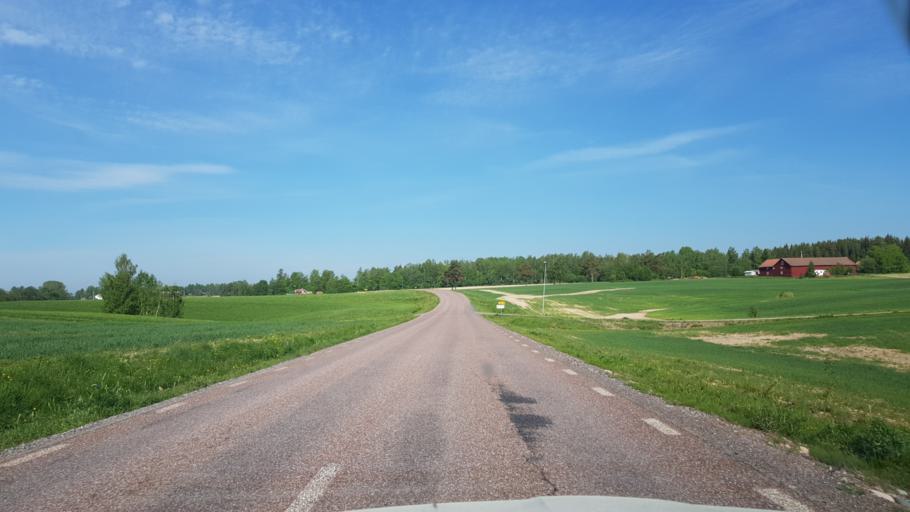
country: SE
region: Dalarna
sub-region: Saters Kommun
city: Saeter
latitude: 60.4248
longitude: 15.6437
